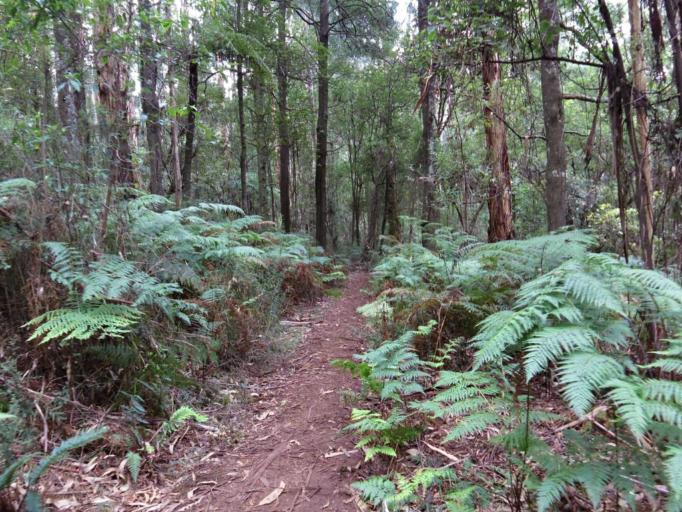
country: AU
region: Victoria
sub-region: Yarra Ranges
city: Olinda
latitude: -37.8431
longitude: 145.3798
